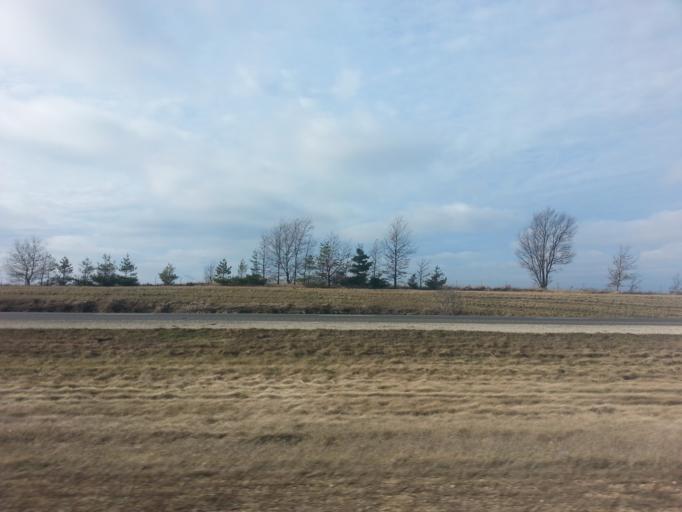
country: US
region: Illinois
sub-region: Ogle County
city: Davis Junction
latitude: 42.1471
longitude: -89.0233
